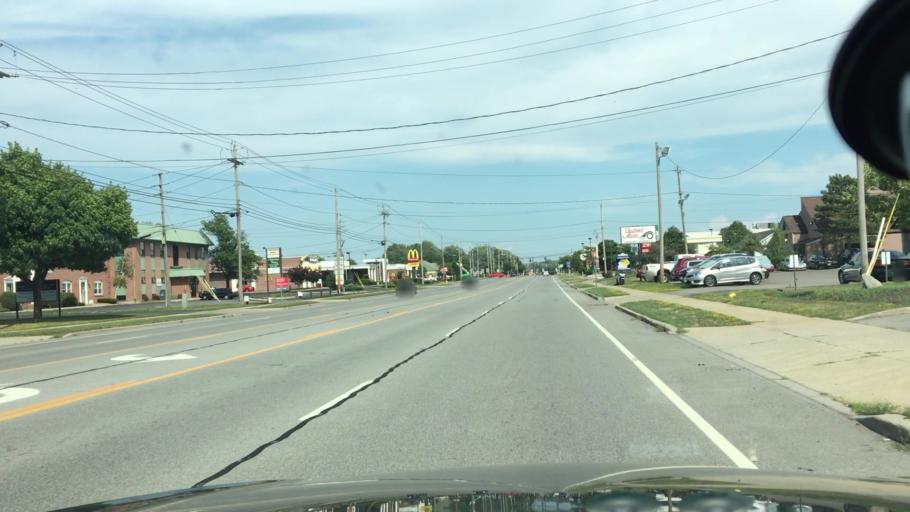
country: US
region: New York
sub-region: Erie County
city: Williamsville
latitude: 42.9785
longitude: -78.7435
